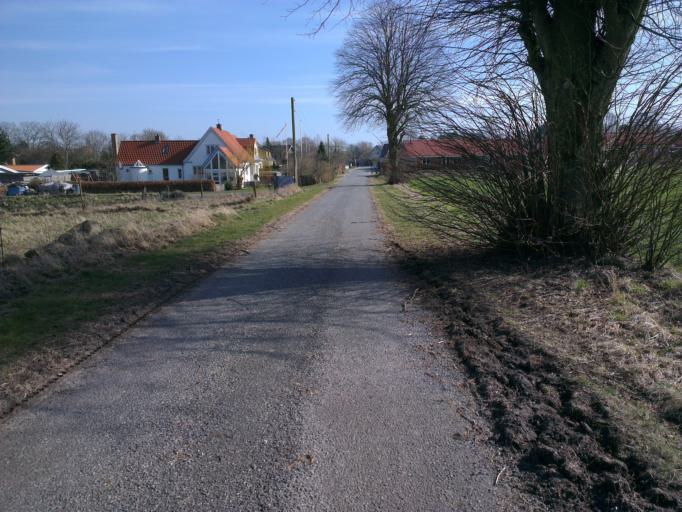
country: DK
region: Capital Region
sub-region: Frederikssund Kommune
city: Jaegerspris
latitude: 55.8065
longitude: 11.9784
